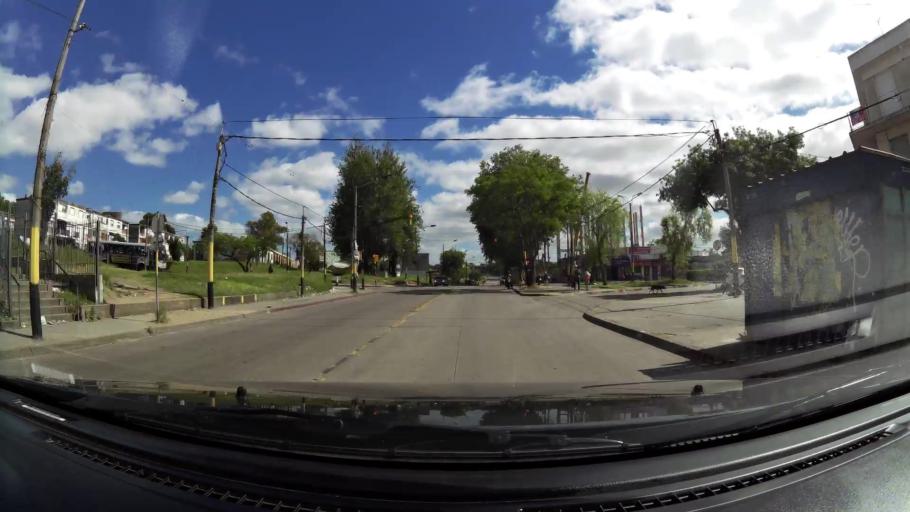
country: UY
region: Canelones
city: Paso de Carrasco
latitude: -34.8813
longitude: -56.1115
